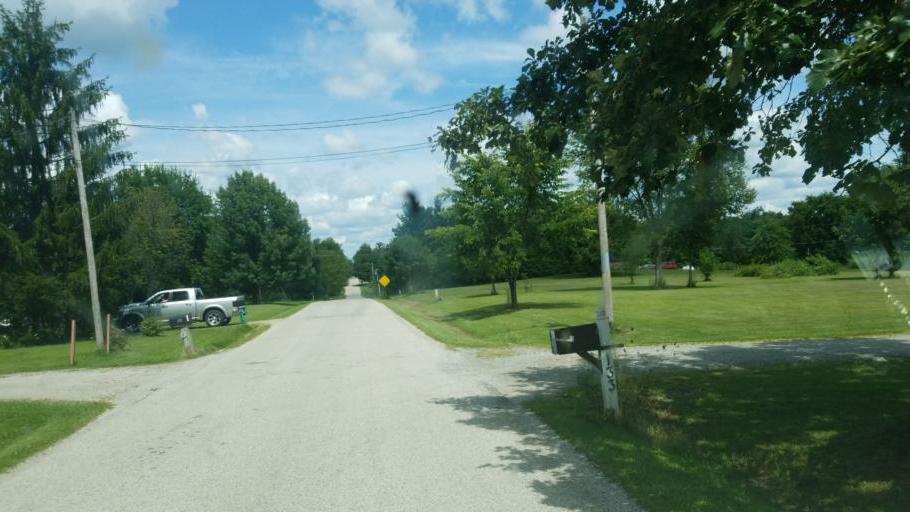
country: US
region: Ohio
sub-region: Knox County
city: Centerburg
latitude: 40.3556
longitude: -82.7787
